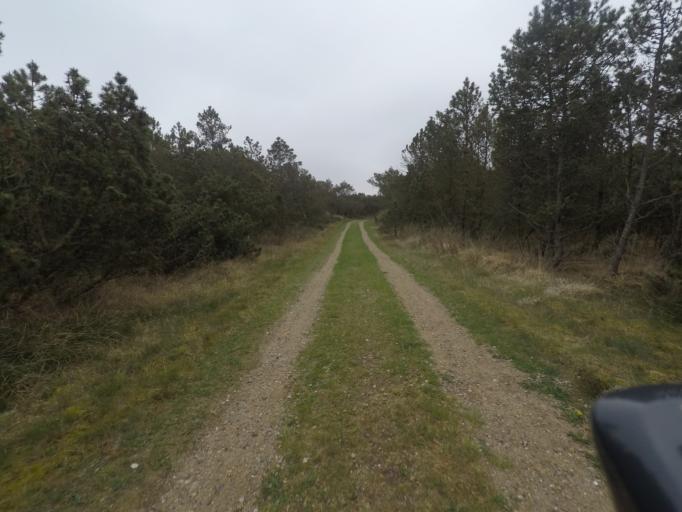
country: DE
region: Schleswig-Holstein
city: List
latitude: 55.1228
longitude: 8.5224
